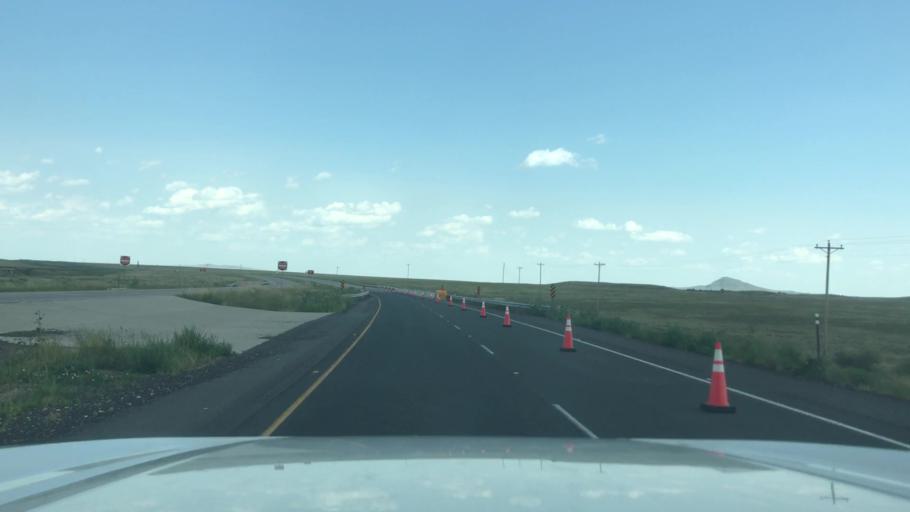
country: US
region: New Mexico
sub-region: Union County
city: Clayton
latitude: 36.6158
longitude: -103.6874
